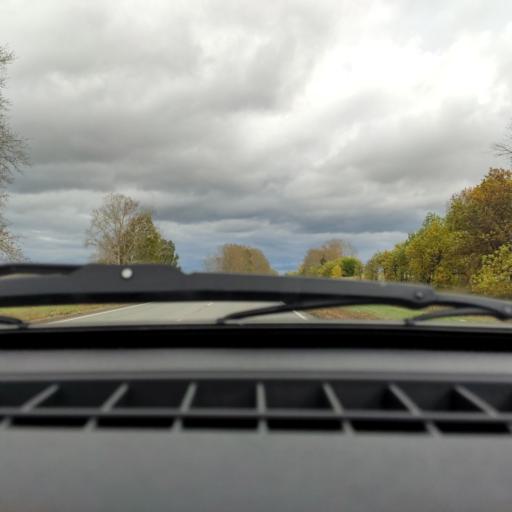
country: RU
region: Bashkortostan
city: Shafranovo
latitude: 54.0142
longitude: 54.8120
